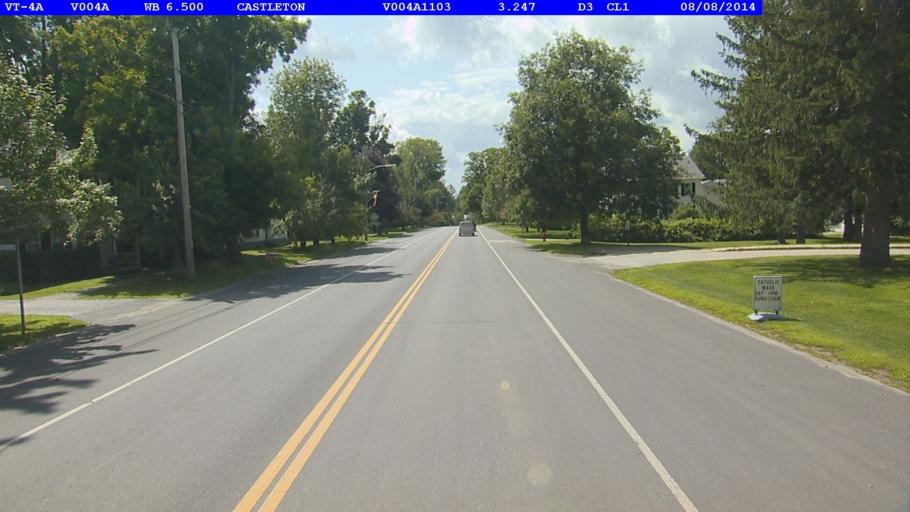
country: US
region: Vermont
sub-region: Rutland County
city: Castleton
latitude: 43.6110
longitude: -73.1809
